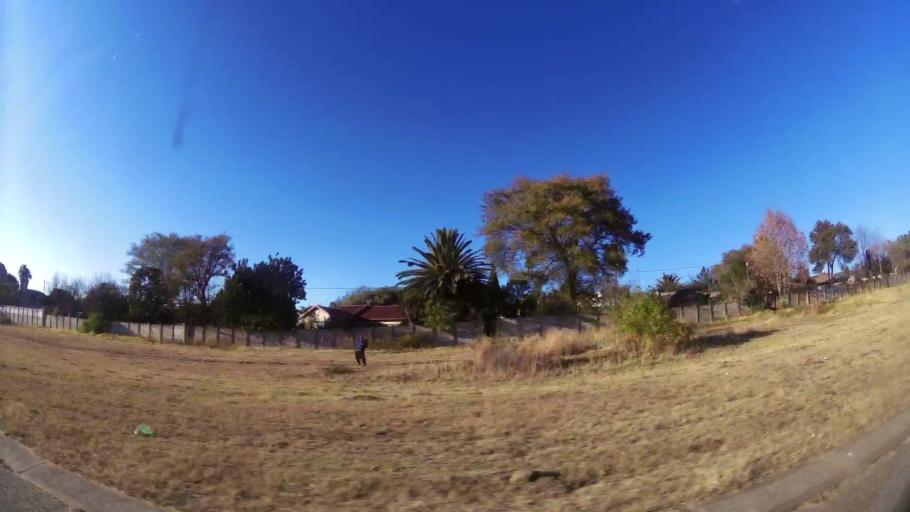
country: ZA
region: Gauteng
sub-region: City of Tshwane Metropolitan Municipality
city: Centurion
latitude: -25.8993
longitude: 28.1416
